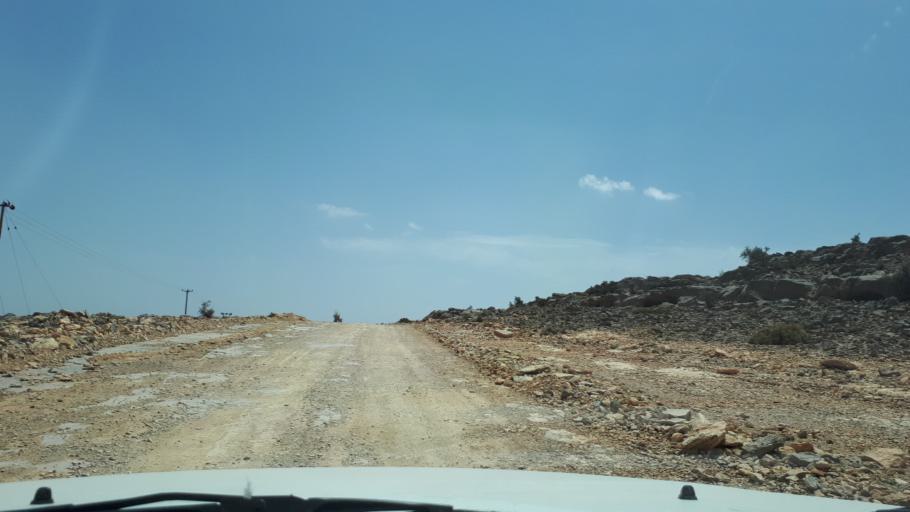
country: OM
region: Muhafazat ad Dakhiliyah
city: Bahla'
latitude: 23.2018
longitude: 57.2007
